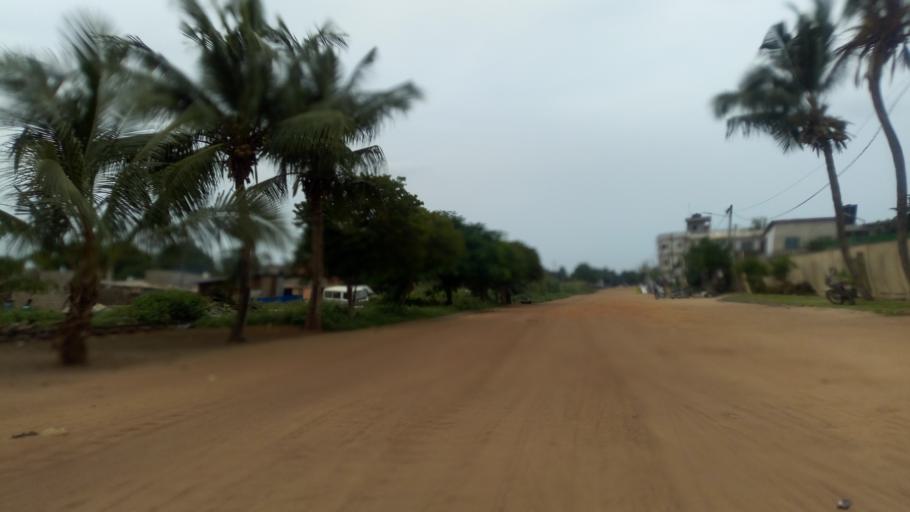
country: TG
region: Maritime
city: Lome
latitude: 6.1818
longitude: 1.1834
